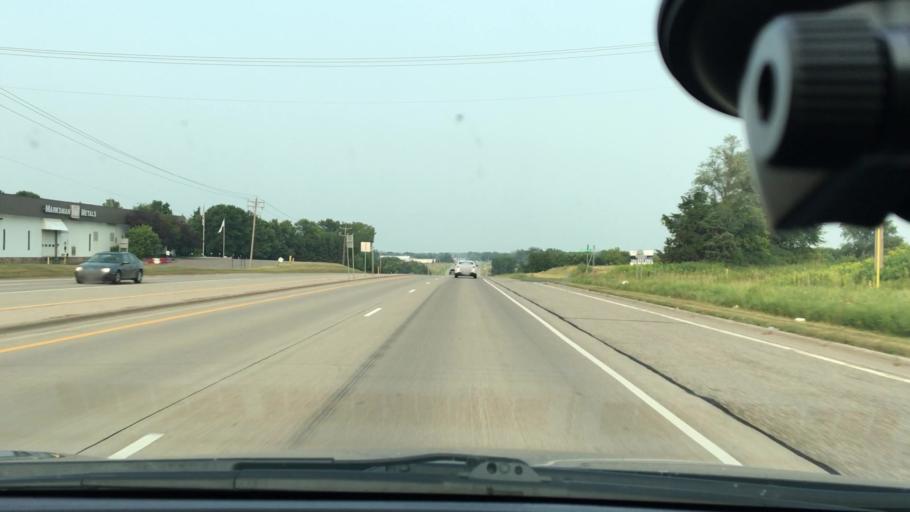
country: US
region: Minnesota
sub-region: Wright County
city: Saint Michael
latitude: 45.2112
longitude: -93.6381
